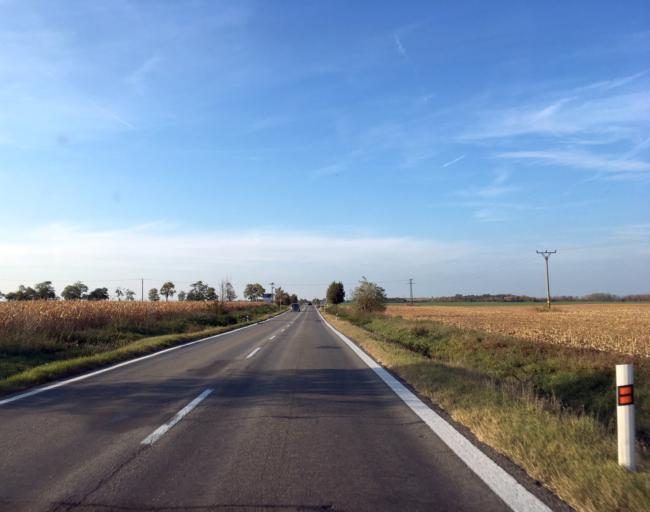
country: SK
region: Nitriansky
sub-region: Okres Nove Zamky
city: Nove Zamky
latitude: 48.0374
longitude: 18.1252
